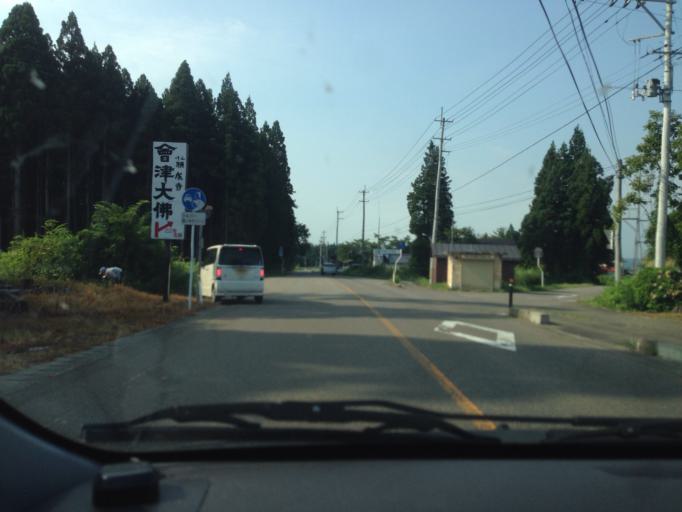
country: JP
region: Fukushima
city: Kitakata
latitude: 37.7164
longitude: 139.8798
